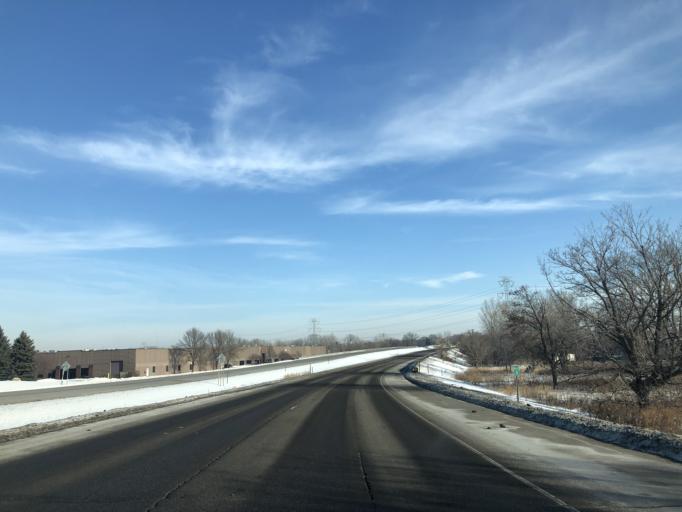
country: US
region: Minnesota
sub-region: Hennepin County
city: Saint Anthony
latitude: 45.0374
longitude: -93.1954
